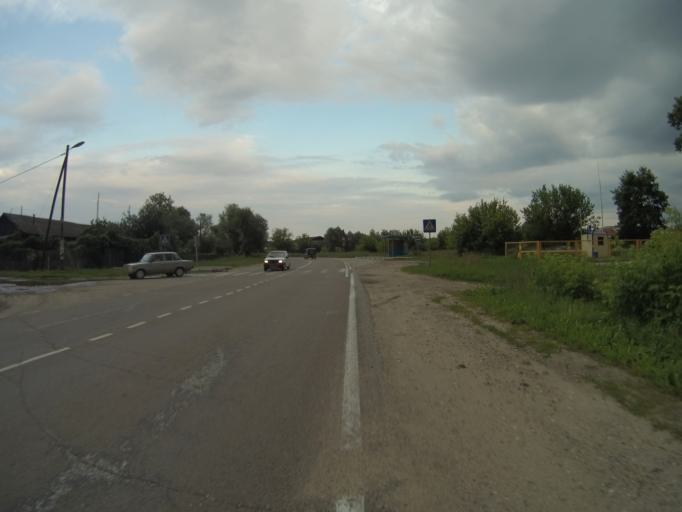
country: RU
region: Vladimir
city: Kameshkovo
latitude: 56.3538
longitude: 40.9179
